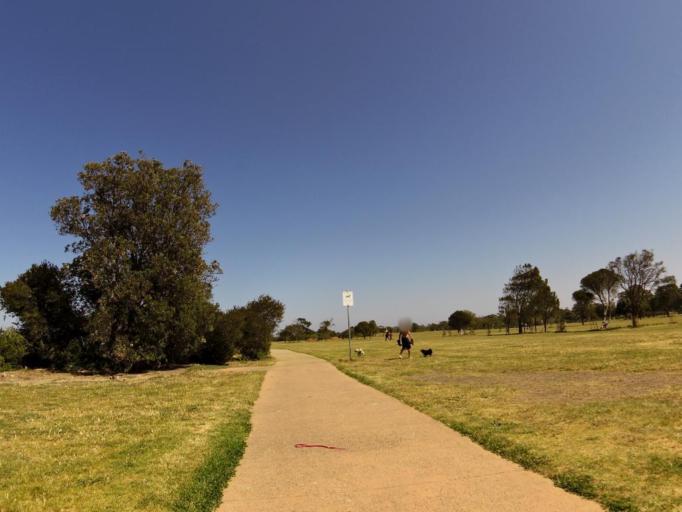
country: AU
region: Victoria
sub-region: Hobsons Bay
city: Altona
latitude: -37.8759
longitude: 144.8127
